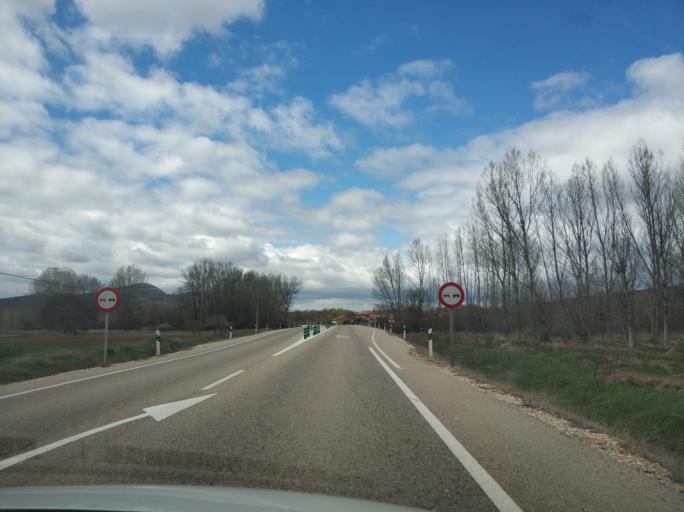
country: ES
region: Castille and Leon
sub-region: Provincia de Burgos
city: Cascajares de la Sierra
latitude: 42.0597
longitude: -3.3971
